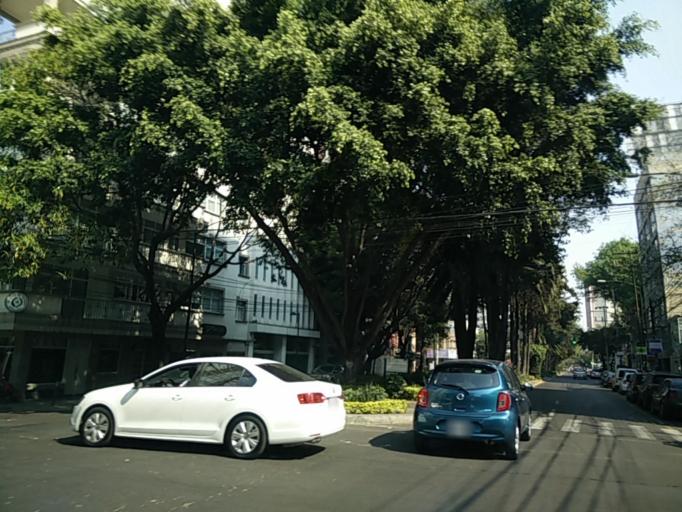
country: MX
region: Mexico City
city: Miguel Hidalgo
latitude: 19.4355
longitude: -99.1881
